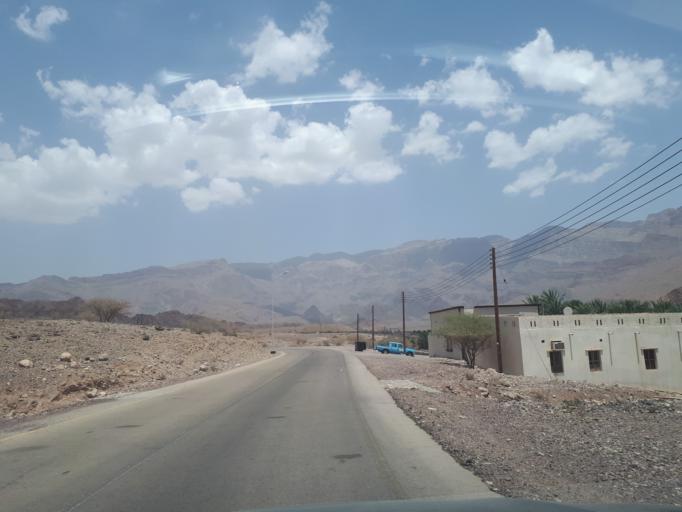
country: OM
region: Ash Sharqiyah
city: Badiyah
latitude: 22.4712
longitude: 59.1075
